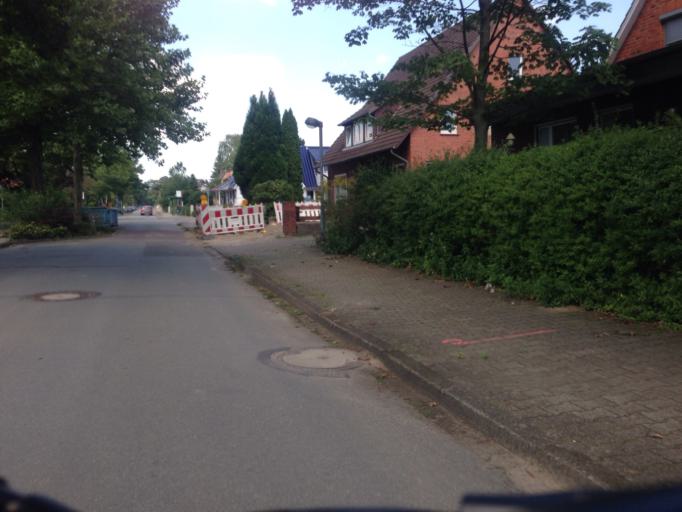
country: DE
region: Lower Saxony
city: Adendorf
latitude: 53.2814
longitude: 10.4326
